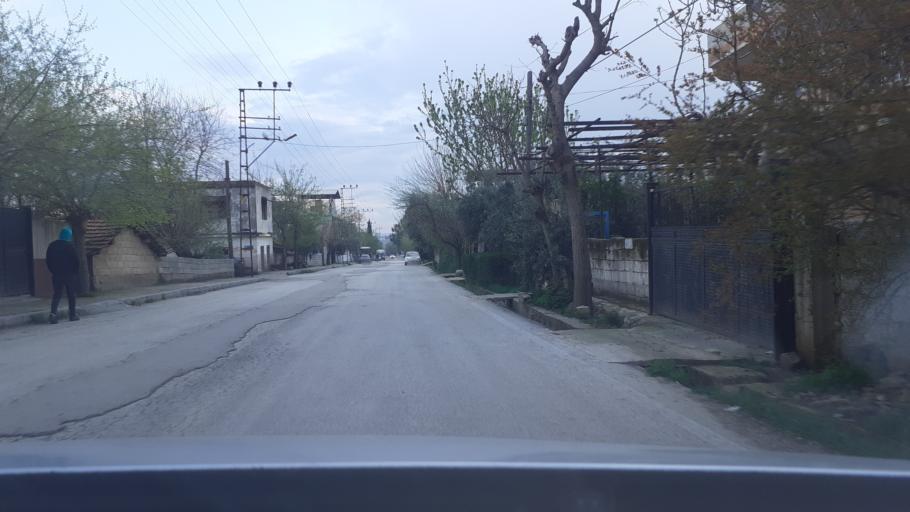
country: TR
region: Hatay
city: Kirikhan
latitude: 36.4867
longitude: 36.3504
